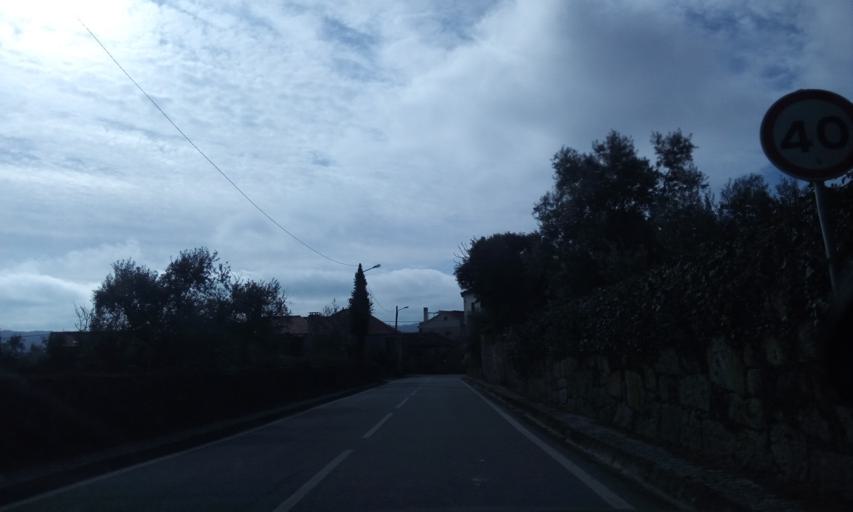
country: PT
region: Guarda
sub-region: Aguiar da Beira
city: Aguiar da Beira
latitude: 40.7341
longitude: -7.5564
